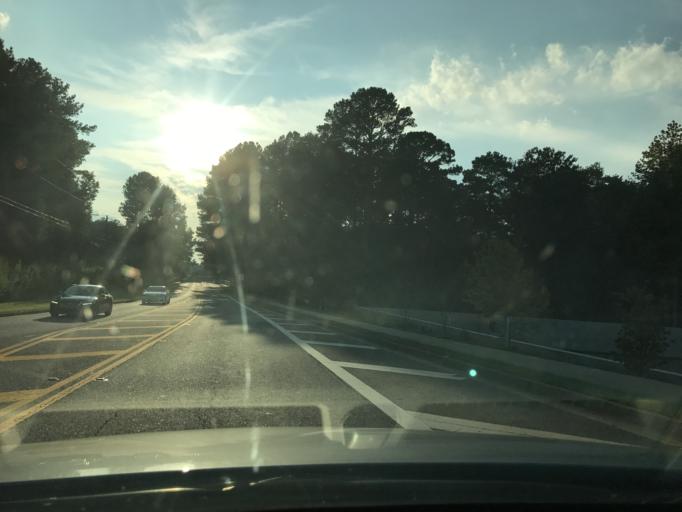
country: US
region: Georgia
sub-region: Fulton County
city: Alpharetta
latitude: 34.0747
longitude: -84.2666
